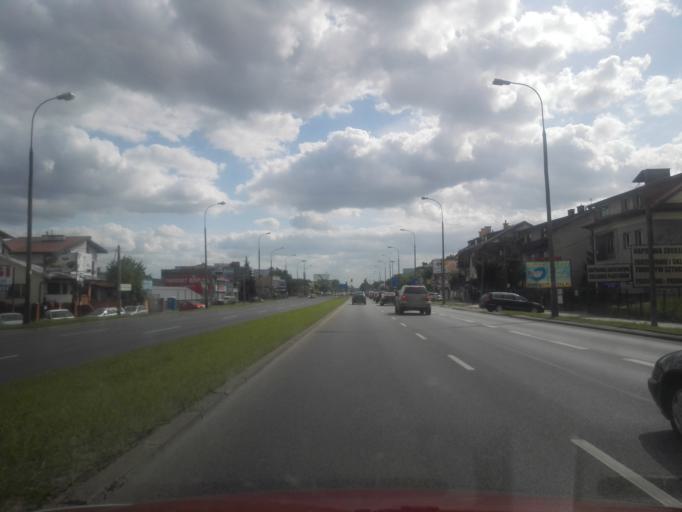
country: PL
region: Masovian Voivodeship
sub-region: Warszawa
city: Targowek
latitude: 52.2823
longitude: 21.0715
